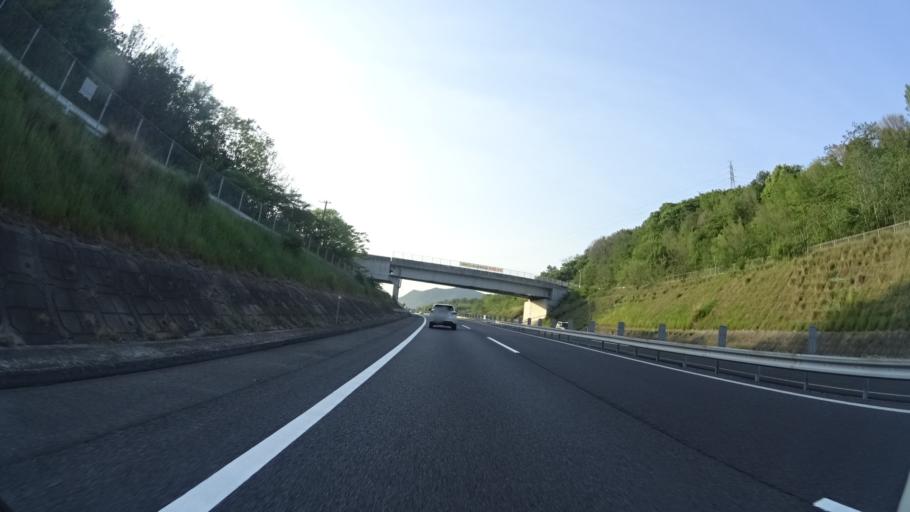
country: JP
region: Kagawa
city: Tadotsu
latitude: 34.2037
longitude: 133.7331
